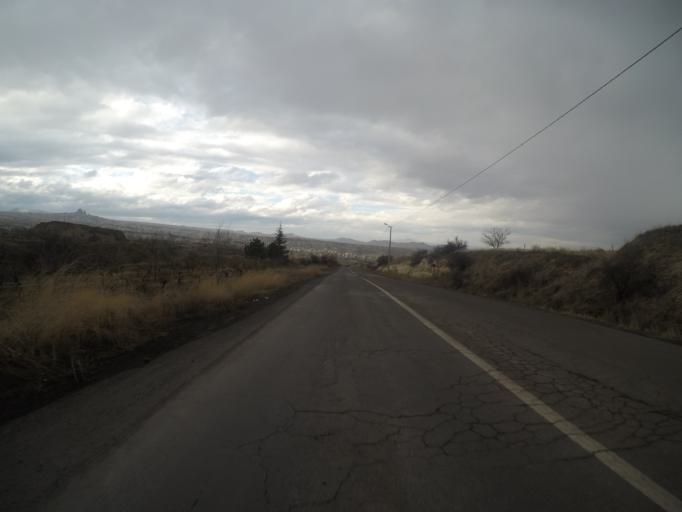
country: TR
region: Nevsehir
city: Goereme
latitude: 38.6391
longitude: 34.8492
